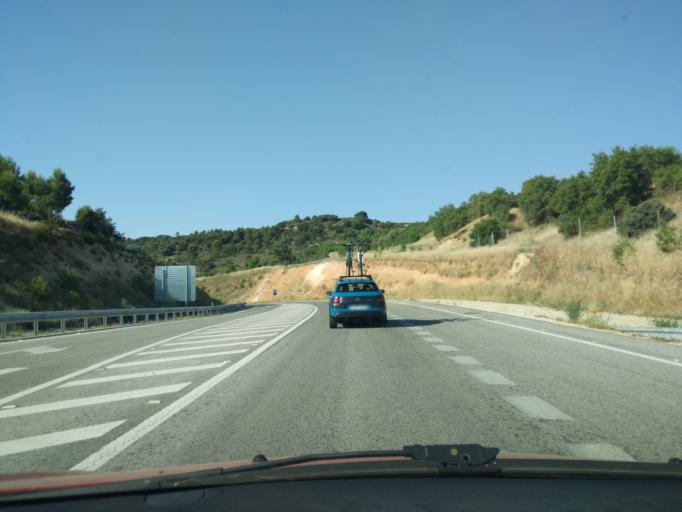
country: ES
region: Madrid
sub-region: Provincia de Madrid
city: Villar del Olmo
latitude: 40.3384
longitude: -3.2415
